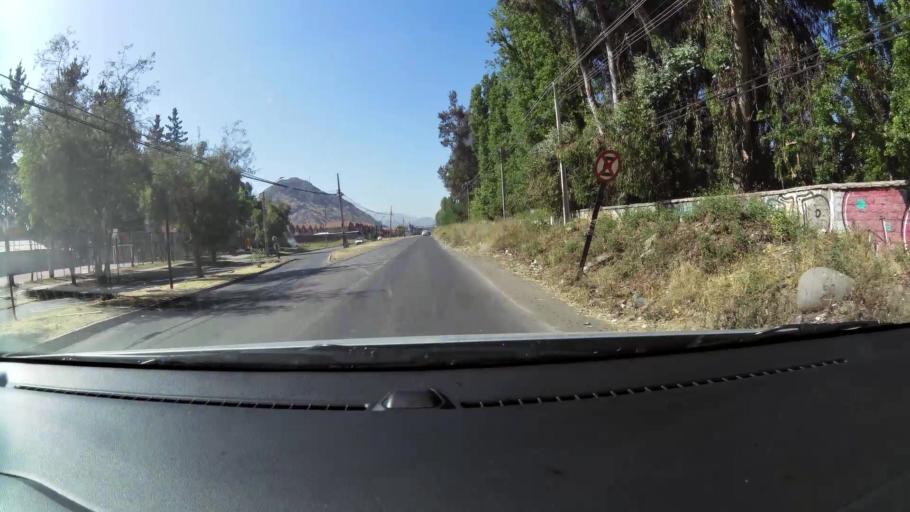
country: CL
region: Santiago Metropolitan
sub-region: Provincia de Maipo
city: San Bernardo
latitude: -33.6128
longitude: -70.6831
